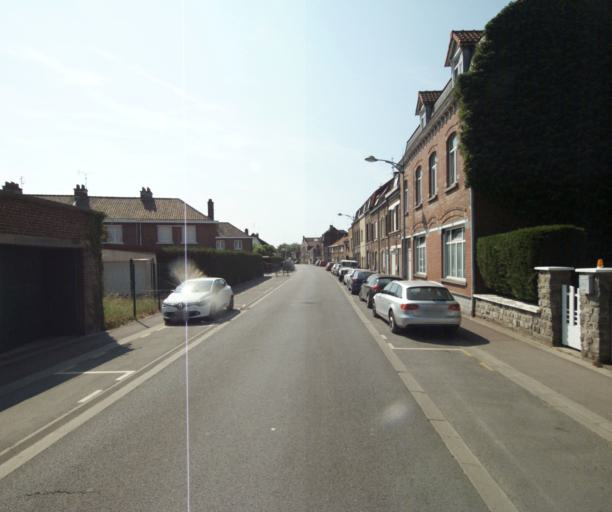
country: FR
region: Nord-Pas-de-Calais
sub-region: Departement du Nord
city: Comines
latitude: 50.7585
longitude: 3.0032
